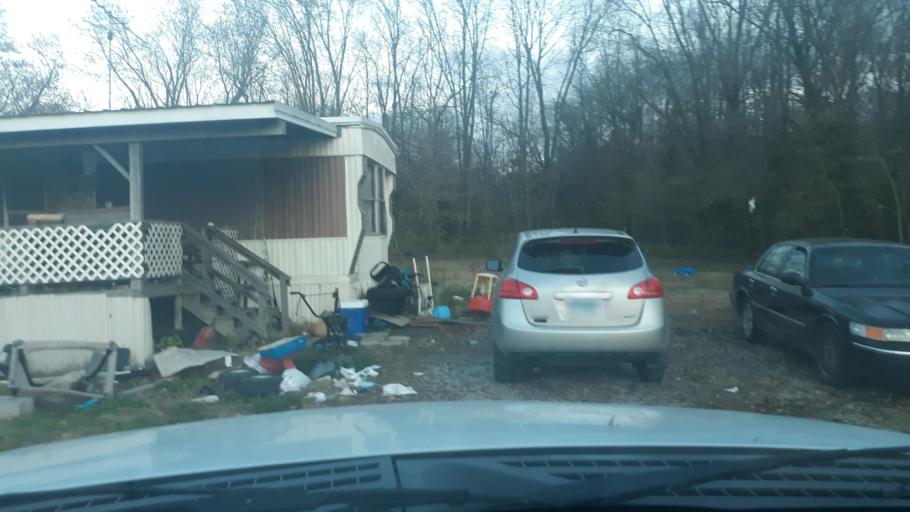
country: US
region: Illinois
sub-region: Saline County
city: Harrisburg
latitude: 37.8469
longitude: -88.6144
